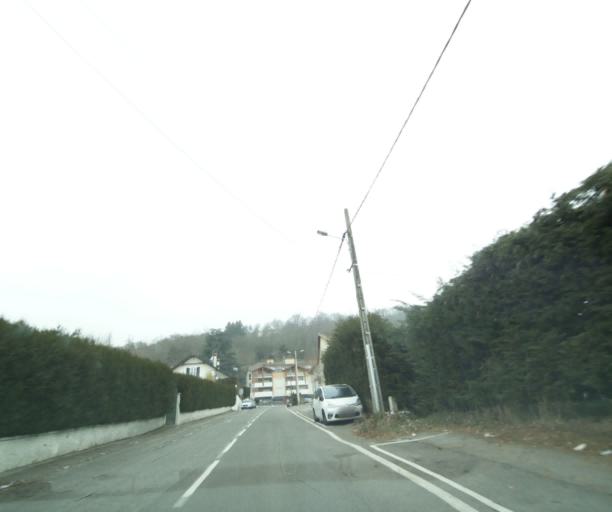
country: FR
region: Rhone-Alpes
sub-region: Departement de la Haute-Savoie
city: Vetraz-Monthoux
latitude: 46.1637
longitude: 6.2380
